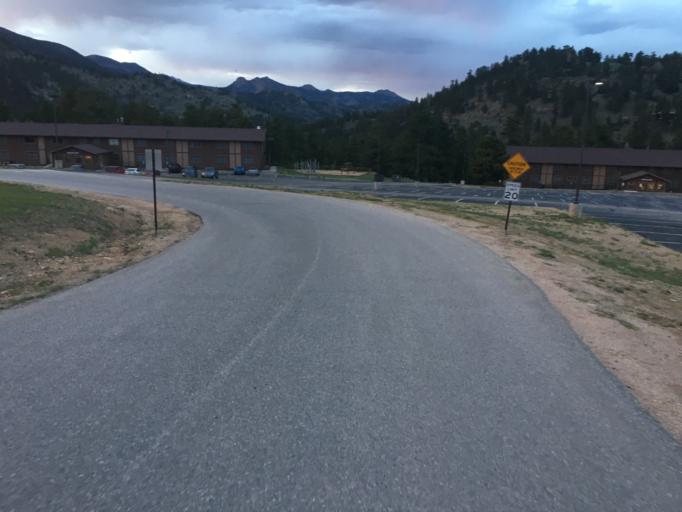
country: US
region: Colorado
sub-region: Larimer County
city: Estes Park
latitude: 40.3398
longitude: -105.5695
